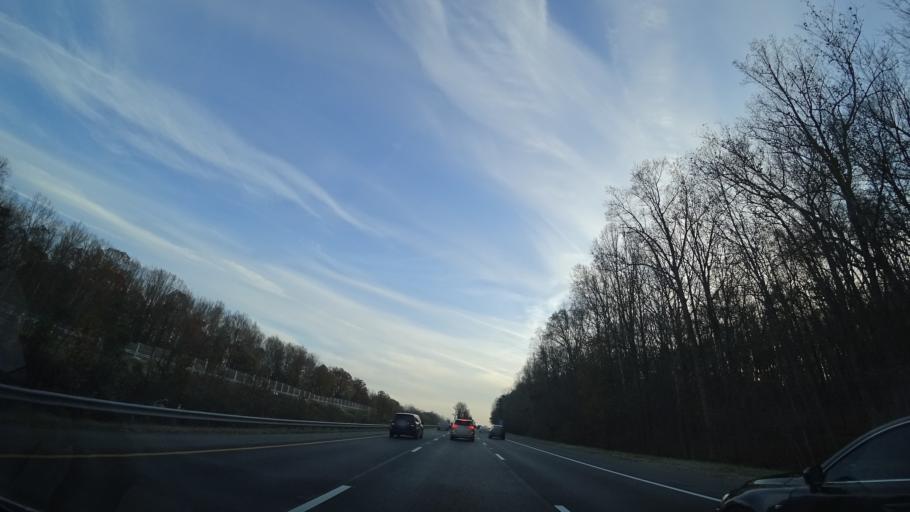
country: US
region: Virginia
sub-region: Stafford County
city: Aquia Harbour
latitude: 38.5020
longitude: -77.3804
